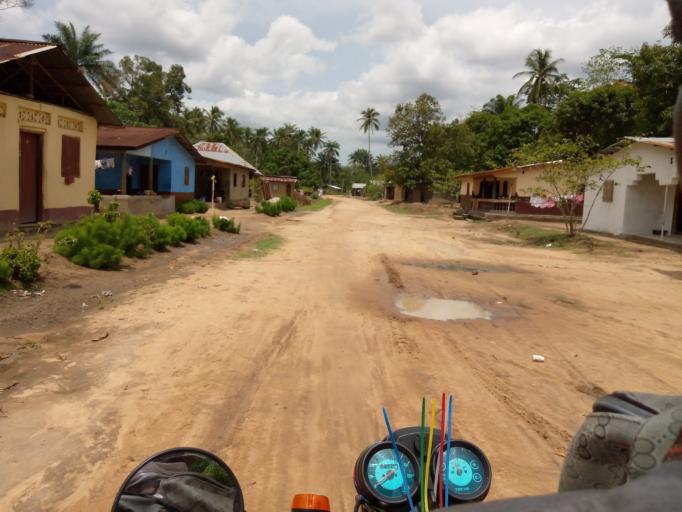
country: SL
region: Western Area
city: Waterloo
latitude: 8.3136
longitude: -12.9420
